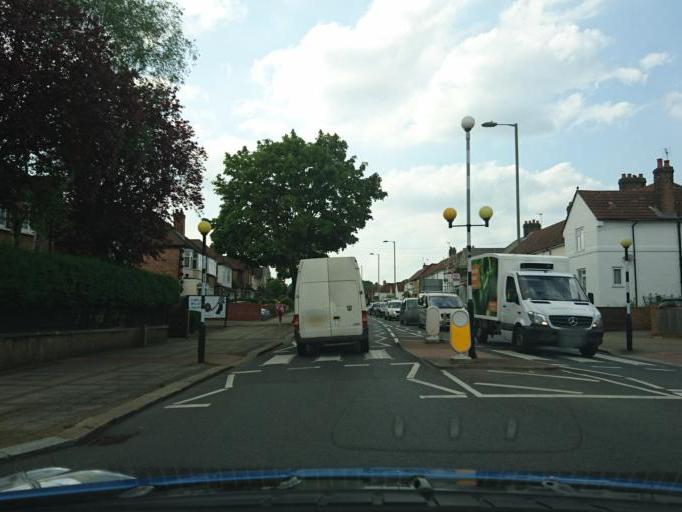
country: GB
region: England
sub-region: Greater London
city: Hadley Wood
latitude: 51.6276
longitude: -0.1619
